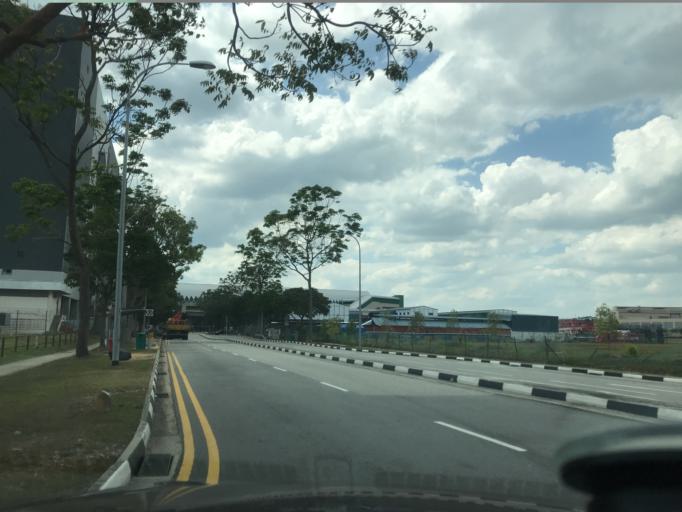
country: MY
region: Johor
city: Johor Bahru
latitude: 1.3383
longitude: 103.6386
